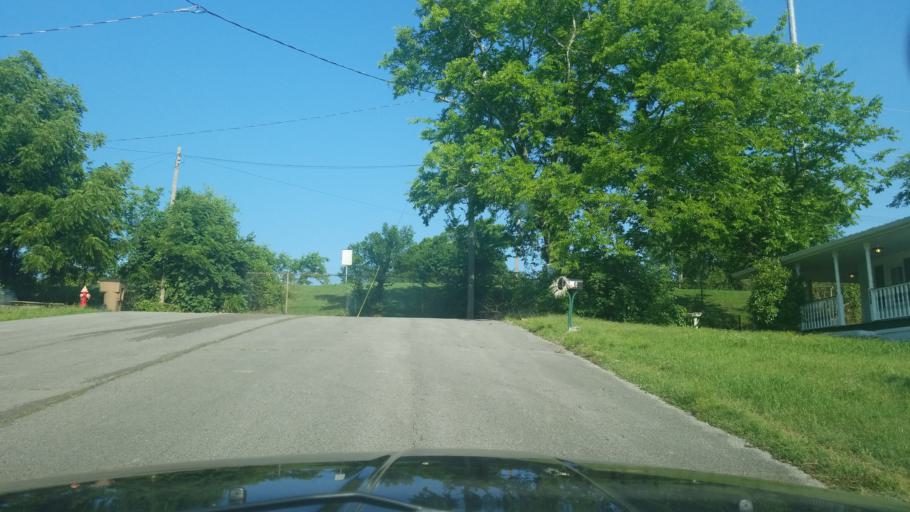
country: US
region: Tennessee
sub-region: Davidson County
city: Oak Hill
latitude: 36.1018
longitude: -86.7437
